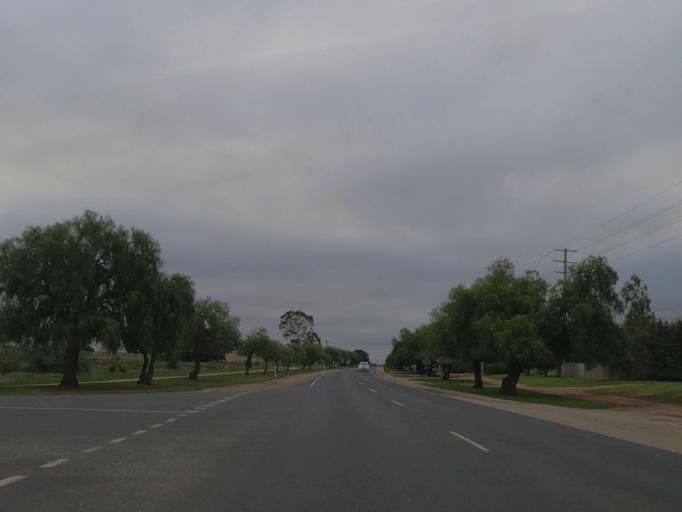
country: AU
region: Victoria
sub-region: Swan Hill
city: Swan Hill
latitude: -35.4577
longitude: 143.6306
